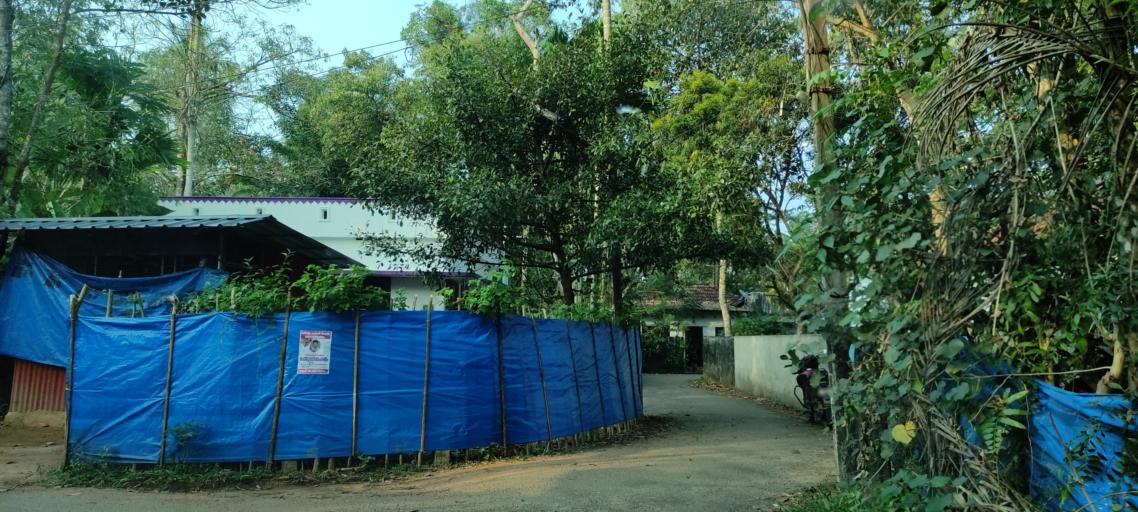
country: IN
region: Kerala
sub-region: Alappuzha
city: Shertallai
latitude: 9.6691
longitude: 76.3558
